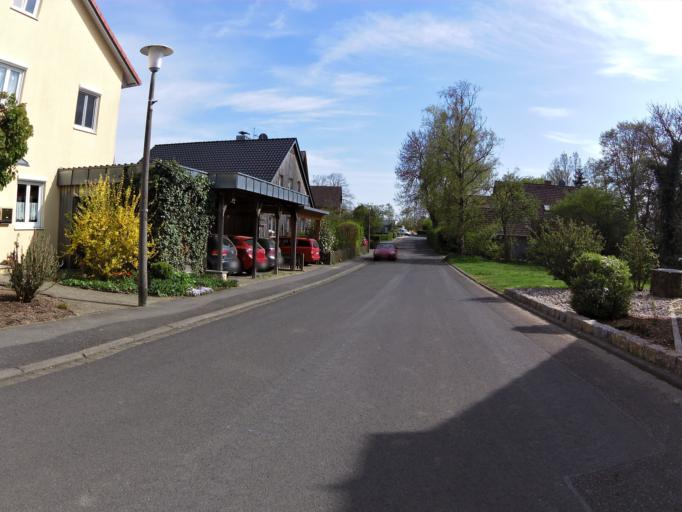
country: DE
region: Bavaria
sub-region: Regierungsbezirk Unterfranken
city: Unterpleichfeld
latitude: 49.8730
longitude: 10.0329
